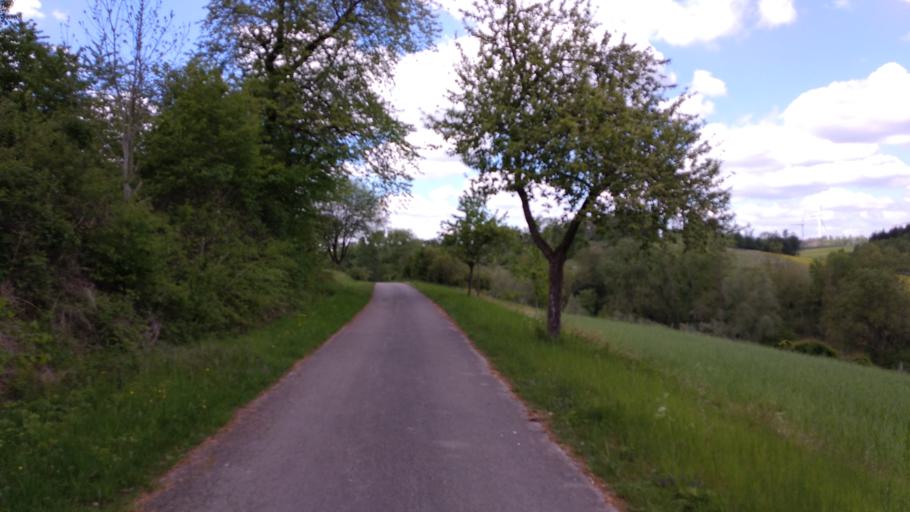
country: DE
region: North Rhine-Westphalia
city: Beverungen
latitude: 51.6786
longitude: 9.3418
